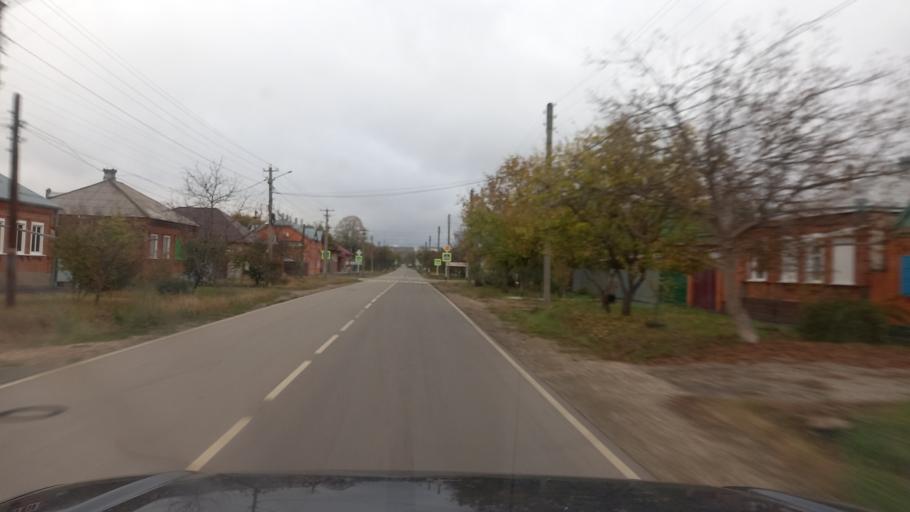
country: RU
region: Adygeya
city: Maykop
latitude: 44.6108
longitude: 40.1214
